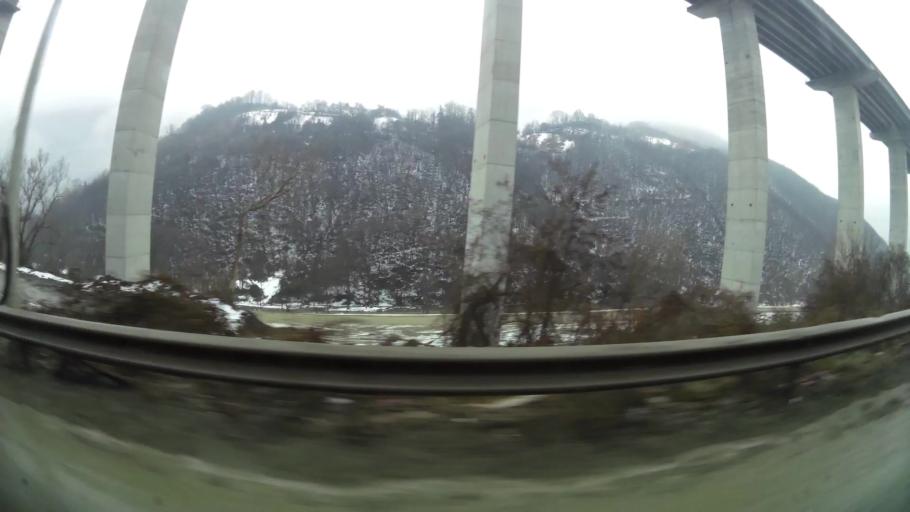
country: XK
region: Ferizaj
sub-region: Hani i Elezit
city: Hani i Elezit
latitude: 42.1710
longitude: 21.2765
